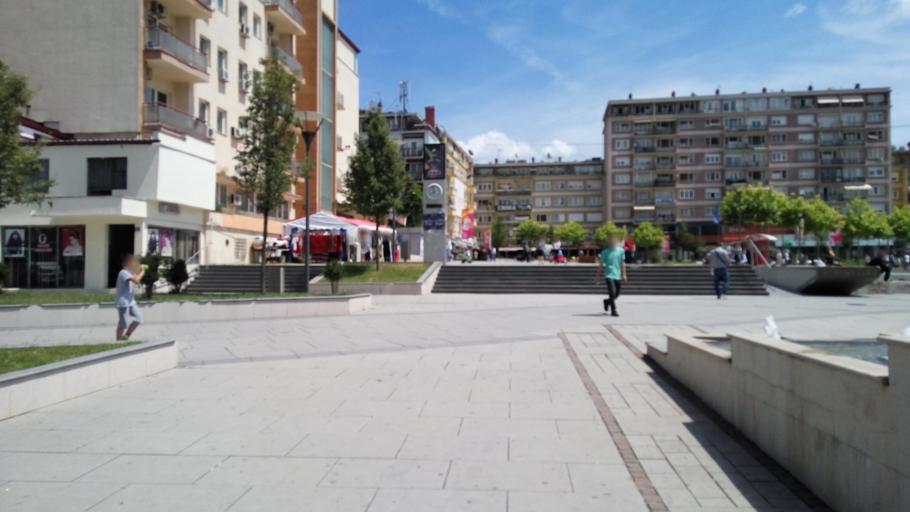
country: XK
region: Pristina
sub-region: Komuna e Prishtines
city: Pristina
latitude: 42.6609
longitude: 21.1604
